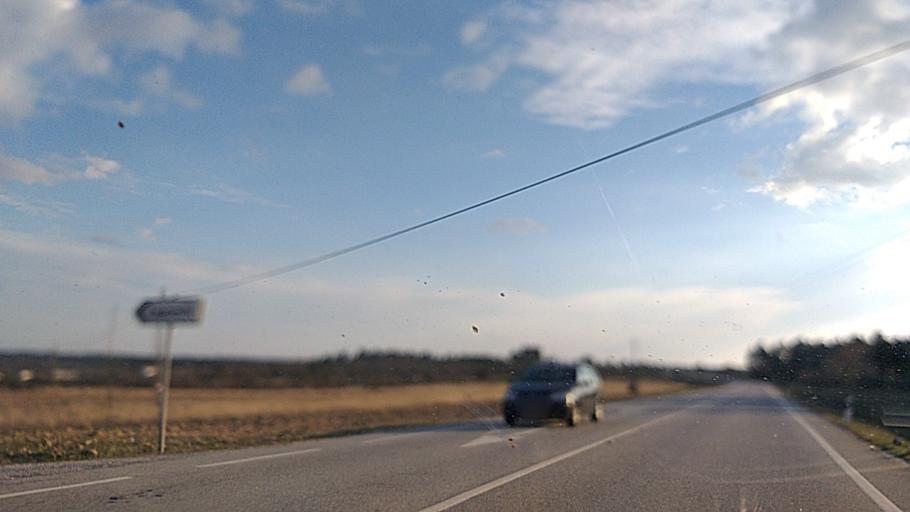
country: PT
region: Guarda
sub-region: Pinhel
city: Pinhel
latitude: 40.6394
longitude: -6.9711
